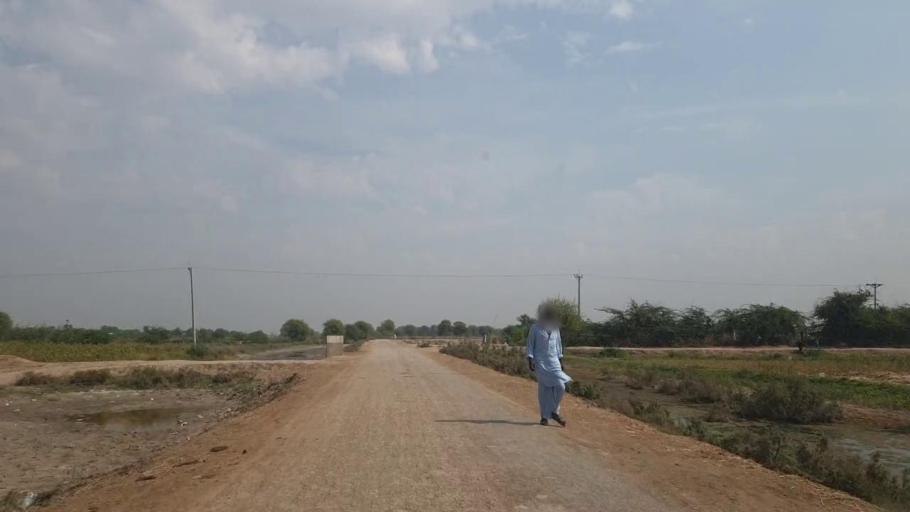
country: PK
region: Sindh
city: Rajo Khanani
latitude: 24.9549
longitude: 68.9838
